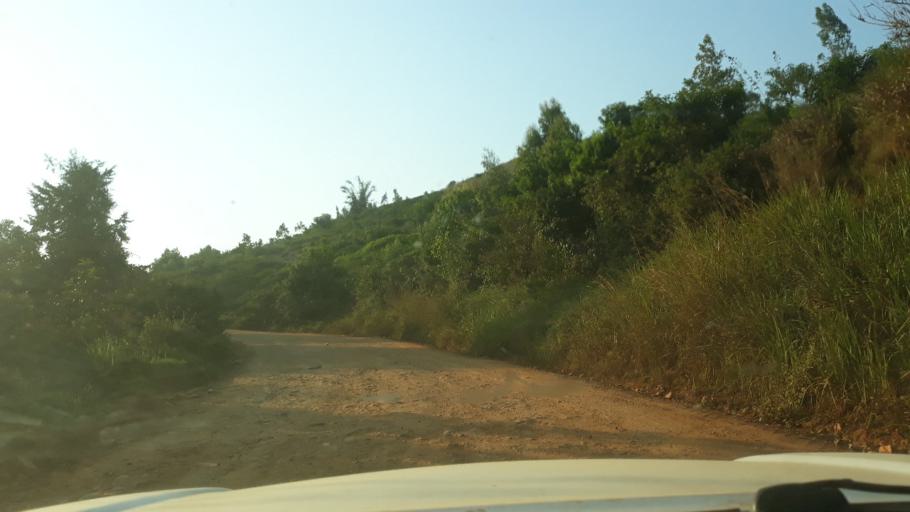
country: RW
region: Western Province
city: Cyangugu
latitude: -2.7028
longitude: 28.9208
